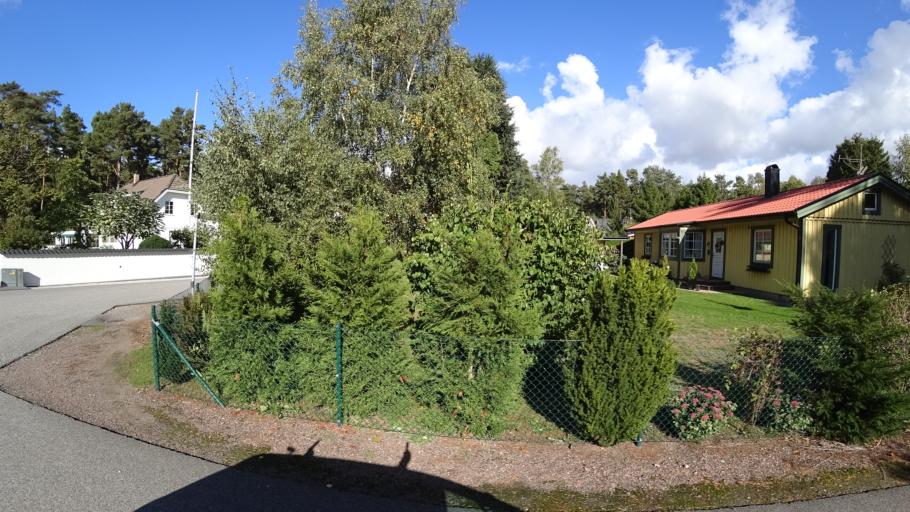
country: SE
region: Skane
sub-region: Kavlinge Kommun
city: Loddekopinge
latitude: 55.7559
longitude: 12.9876
